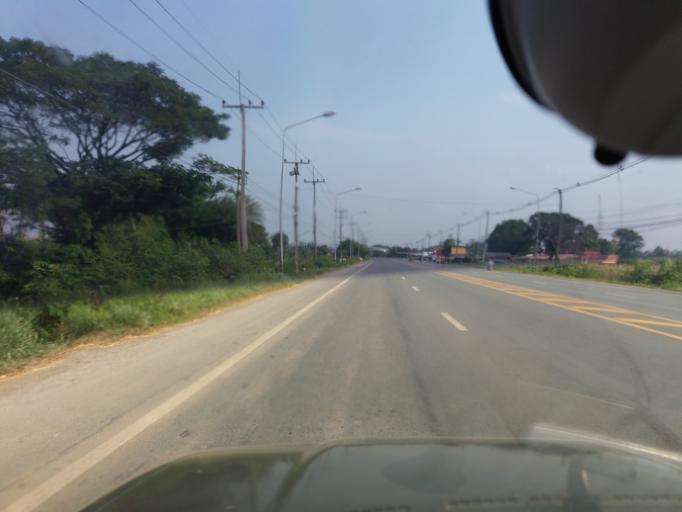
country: TH
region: Sing Buri
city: Sing Buri
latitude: 14.8855
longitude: 100.3754
